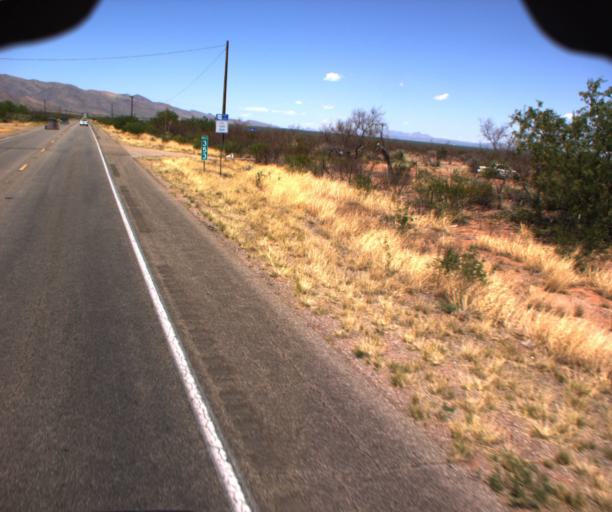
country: US
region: Arizona
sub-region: Cochise County
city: Bisbee
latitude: 31.3924
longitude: -109.7662
